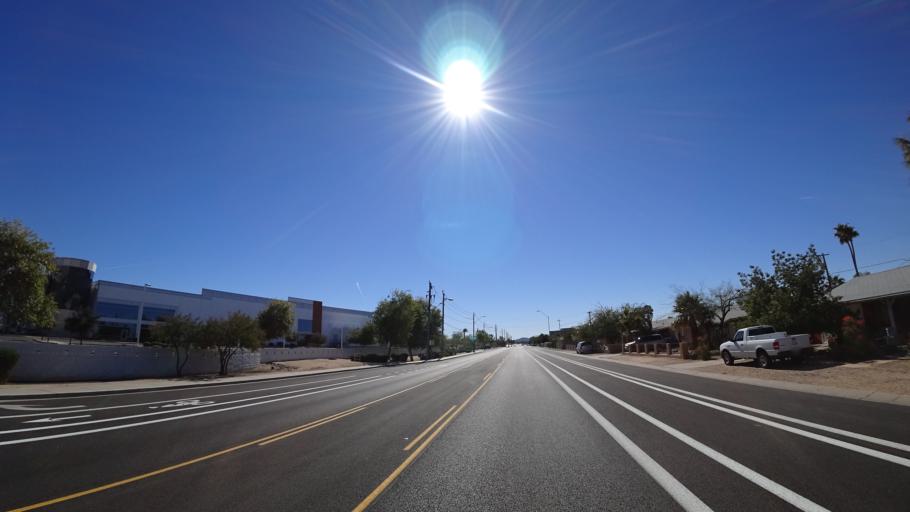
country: US
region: Arizona
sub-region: Maricopa County
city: Tempe Junction
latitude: 33.4559
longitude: -111.9785
